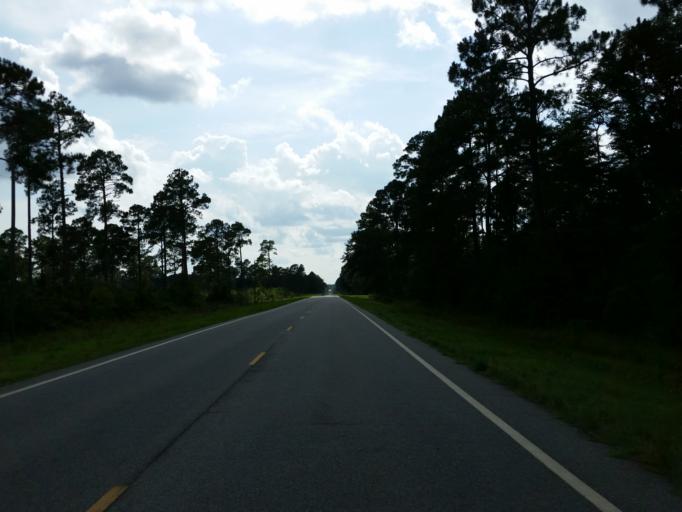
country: US
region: Georgia
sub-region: Lee County
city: Leesburg
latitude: 31.7282
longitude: -83.9680
